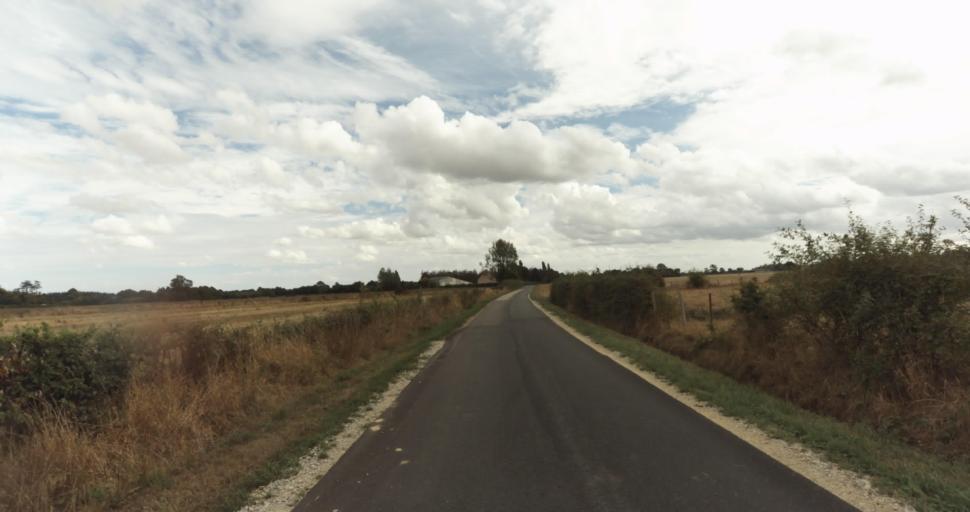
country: FR
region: Lower Normandy
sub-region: Departement de l'Orne
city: Gace
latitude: 48.8871
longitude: 0.3536
